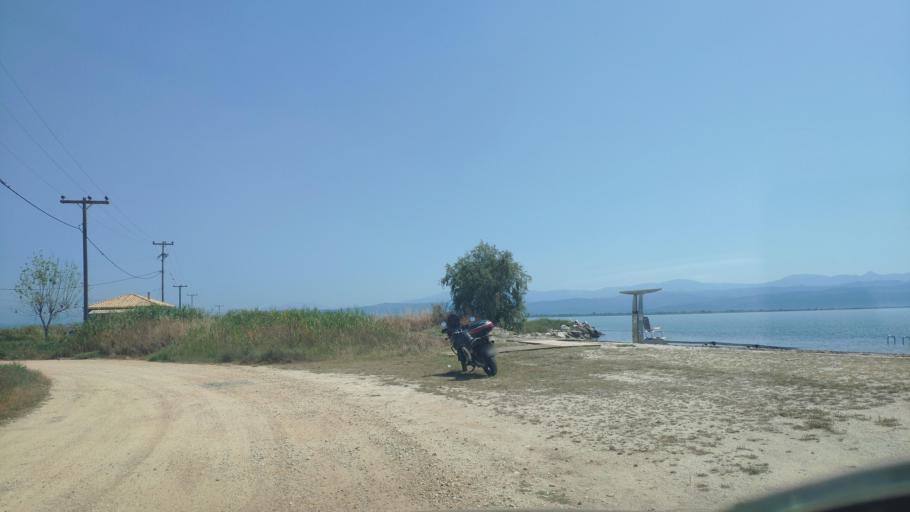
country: GR
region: Epirus
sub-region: Nomos Artas
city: Aneza
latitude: 39.0118
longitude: 20.9259
